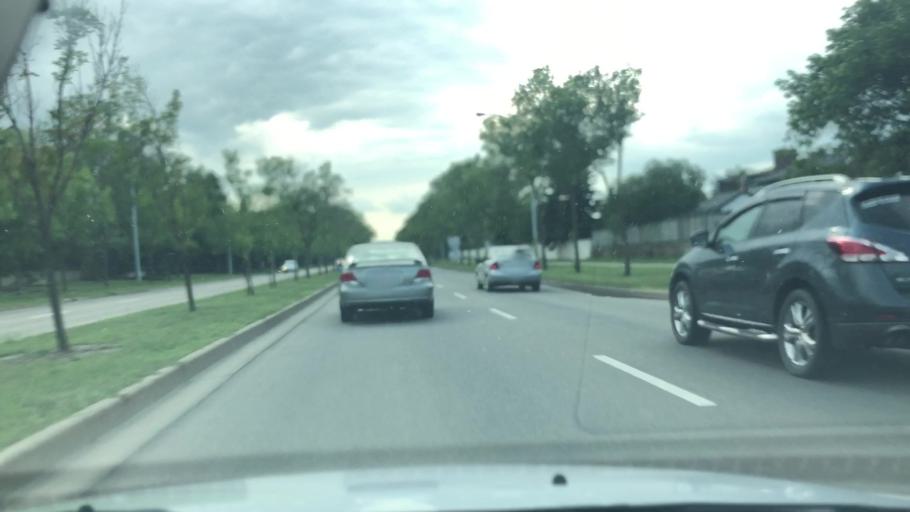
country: CA
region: Alberta
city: Edmonton
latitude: 53.6170
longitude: -113.5332
